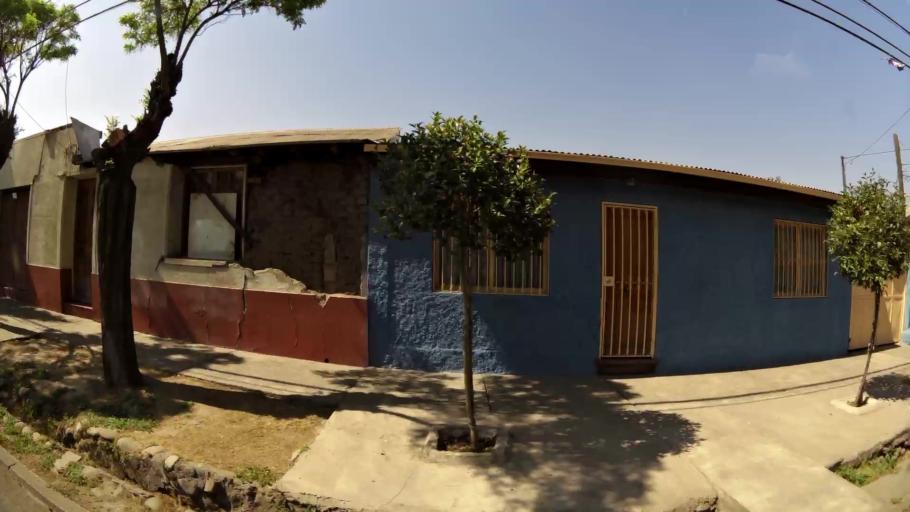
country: CL
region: Santiago Metropolitan
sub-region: Provincia de Maipo
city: San Bernardo
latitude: -33.6017
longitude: -70.7124
